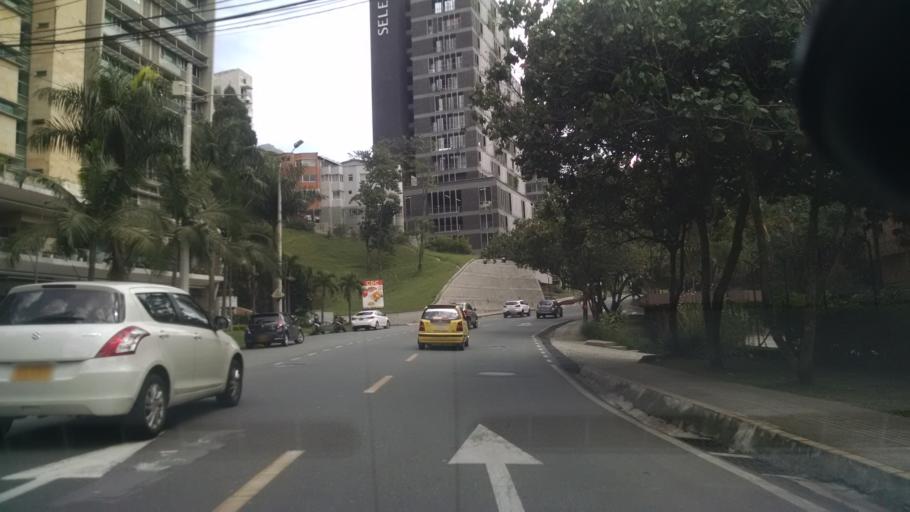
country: CO
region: Antioquia
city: Medellin
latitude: 6.2129
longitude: -75.5596
